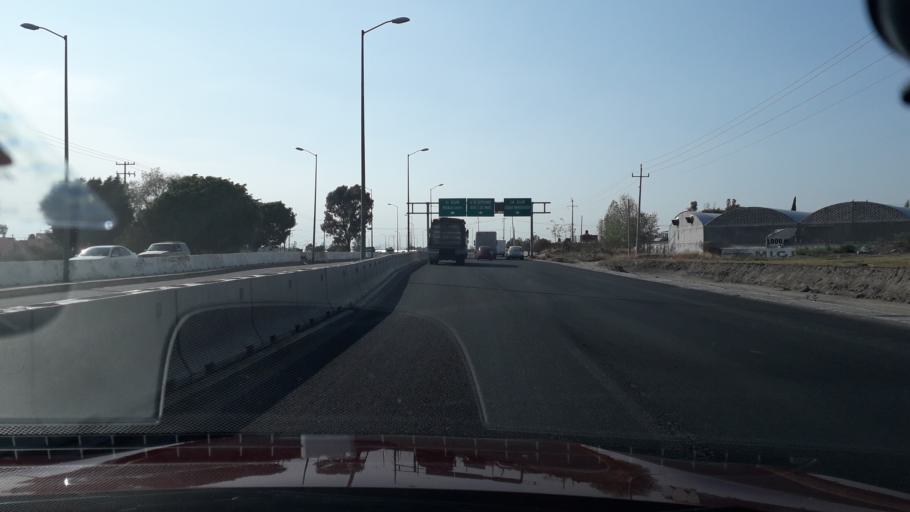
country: MX
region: Puebla
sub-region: Puebla
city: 18 de Marzo
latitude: 18.9763
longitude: -98.2123
